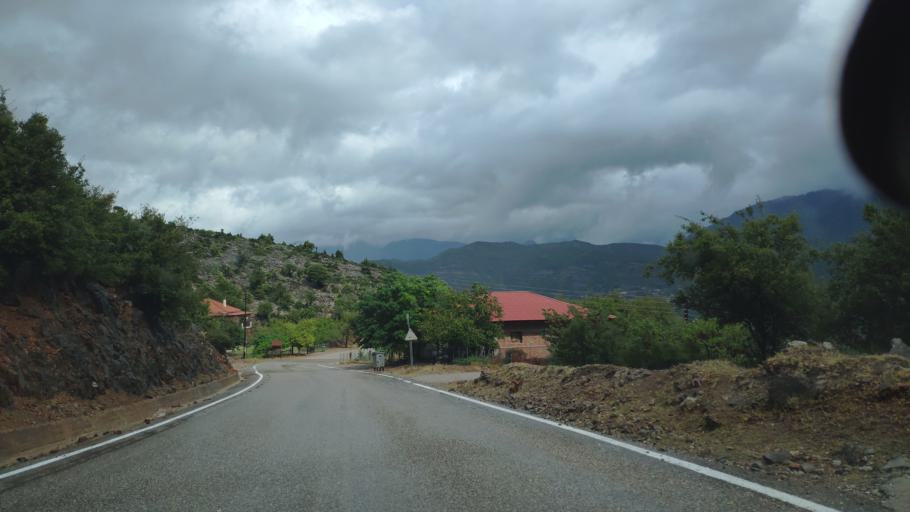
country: GR
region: Thessaly
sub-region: Nomos Kardhitsas
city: Anthiro
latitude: 39.1097
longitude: 21.4075
